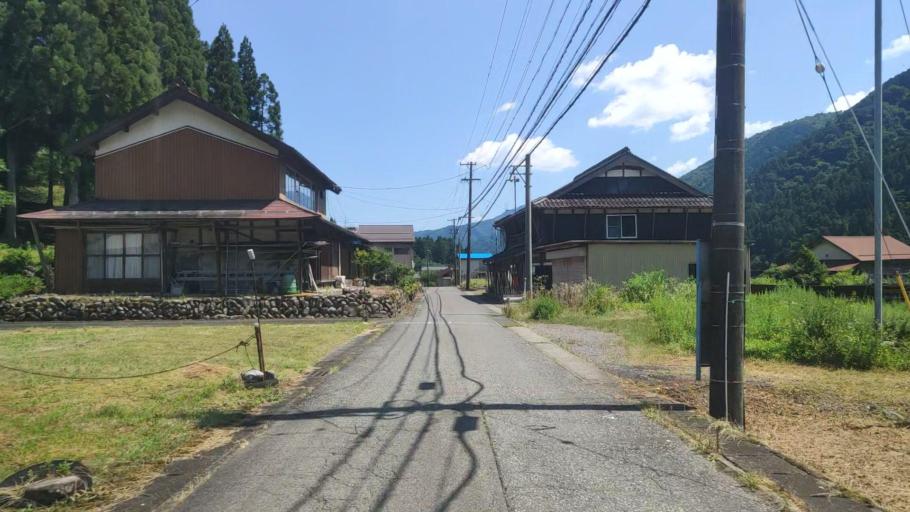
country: JP
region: Gifu
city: Godo
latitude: 35.6790
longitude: 136.5719
